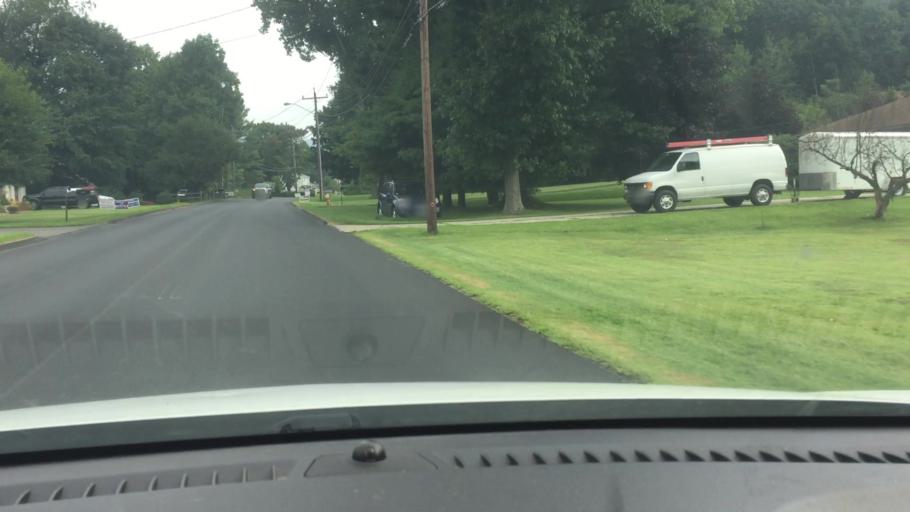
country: US
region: Massachusetts
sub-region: Berkshire County
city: Pittsfield
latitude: 42.4882
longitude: -73.2741
